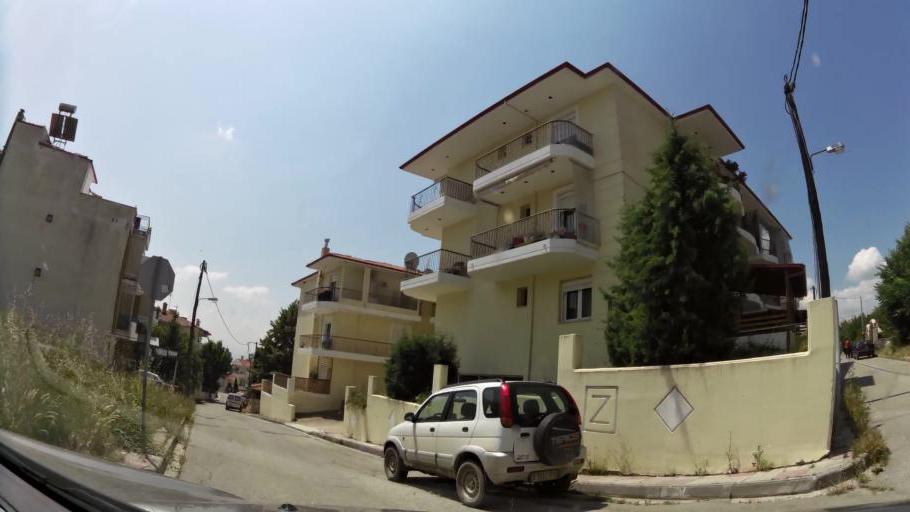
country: GR
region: West Macedonia
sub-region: Nomos Kozanis
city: Kozani
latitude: 40.3022
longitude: 21.7782
